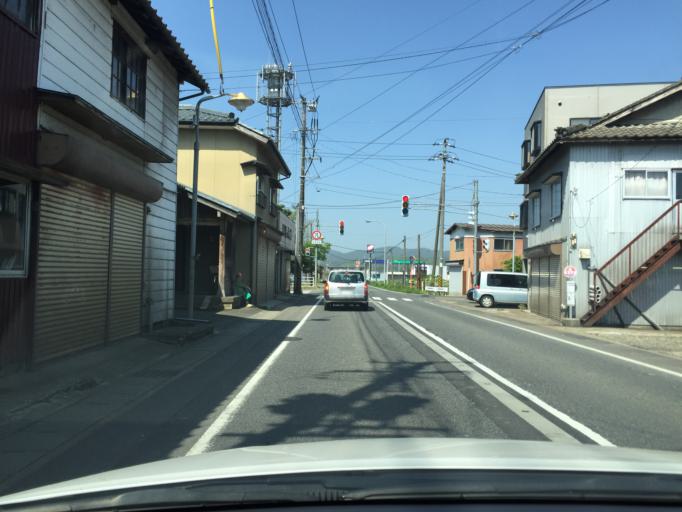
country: JP
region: Niigata
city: Muramatsu
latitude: 37.6882
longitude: 139.1671
